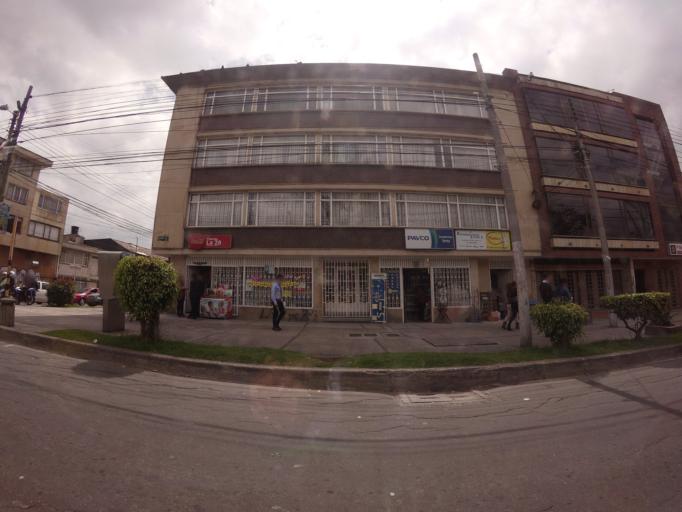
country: CO
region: Bogota D.C.
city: Bogota
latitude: 4.6292
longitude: -74.0782
